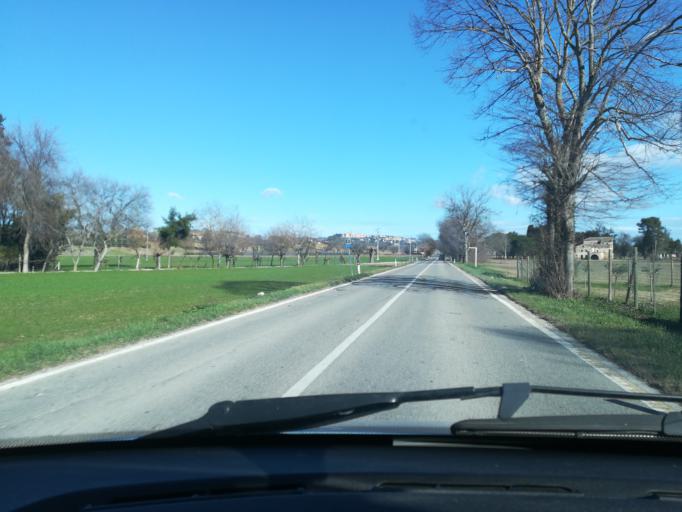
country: IT
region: The Marches
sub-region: Provincia di Macerata
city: Villa Potenza
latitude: 43.3324
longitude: 13.4260
